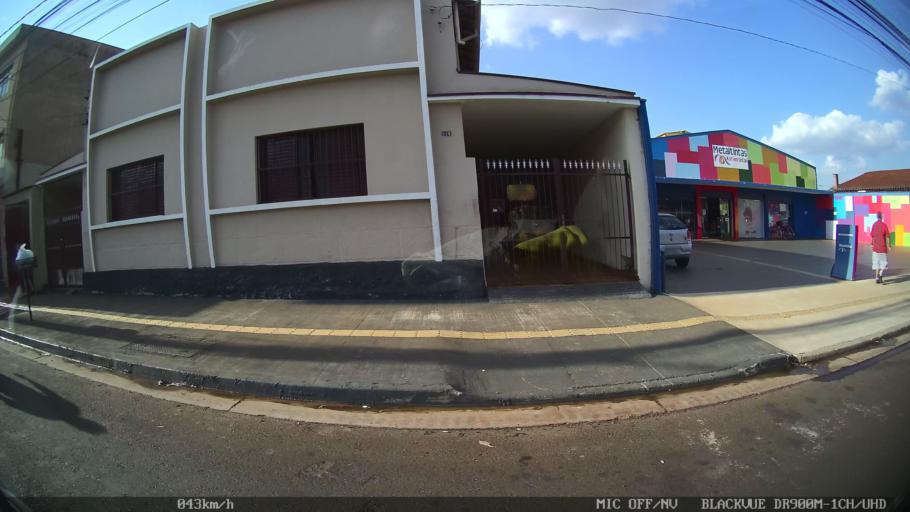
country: BR
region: Sao Paulo
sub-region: Ribeirao Preto
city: Ribeirao Preto
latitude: -21.1571
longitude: -47.8178
